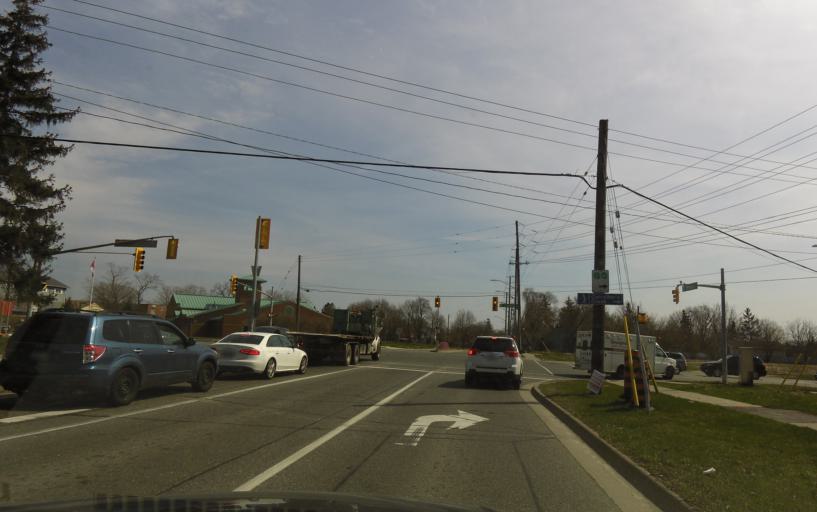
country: CA
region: Ontario
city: Oshawa
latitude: 43.8626
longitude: -78.9349
